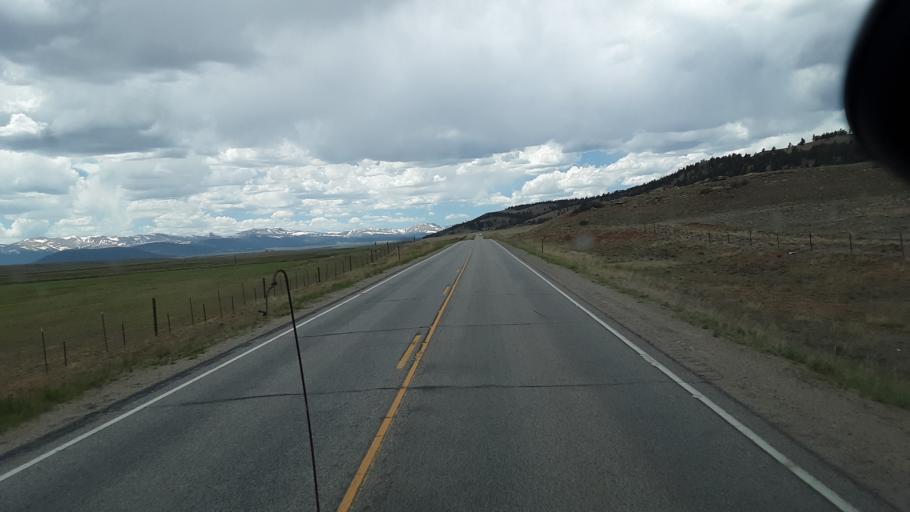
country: US
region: Colorado
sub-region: Park County
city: Fairplay
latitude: 39.0322
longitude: -105.8212
